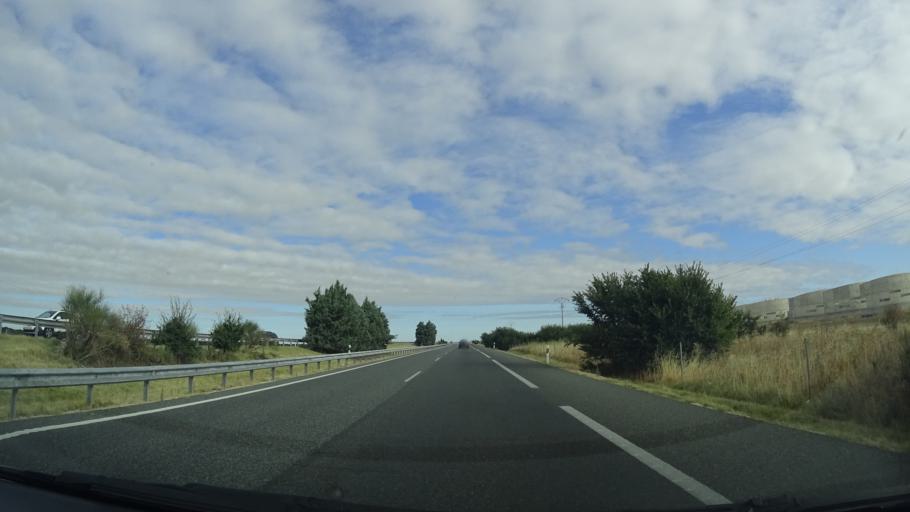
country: ES
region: Castille and Leon
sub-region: Provincia de Valladolid
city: San Vicente del Palacio
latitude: 41.2563
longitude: -4.8747
